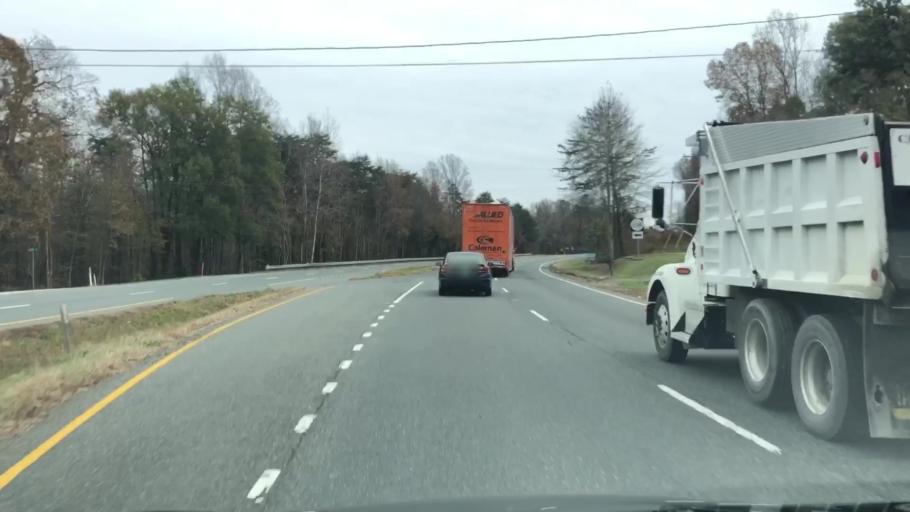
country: US
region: Virginia
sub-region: Stafford County
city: Falmouth
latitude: 38.3903
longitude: -77.5493
